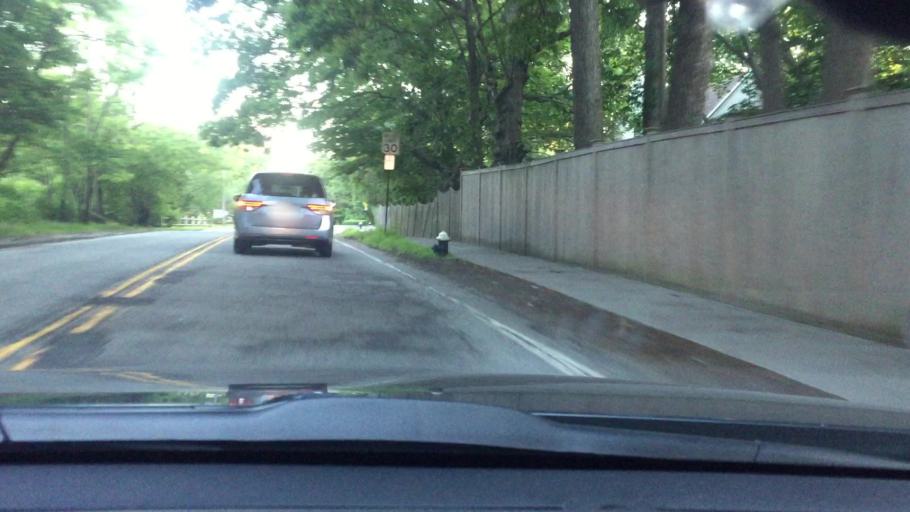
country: US
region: Massachusetts
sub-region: Suffolk County
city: Jamaica Plain
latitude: 42.3144
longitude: -71.1377
